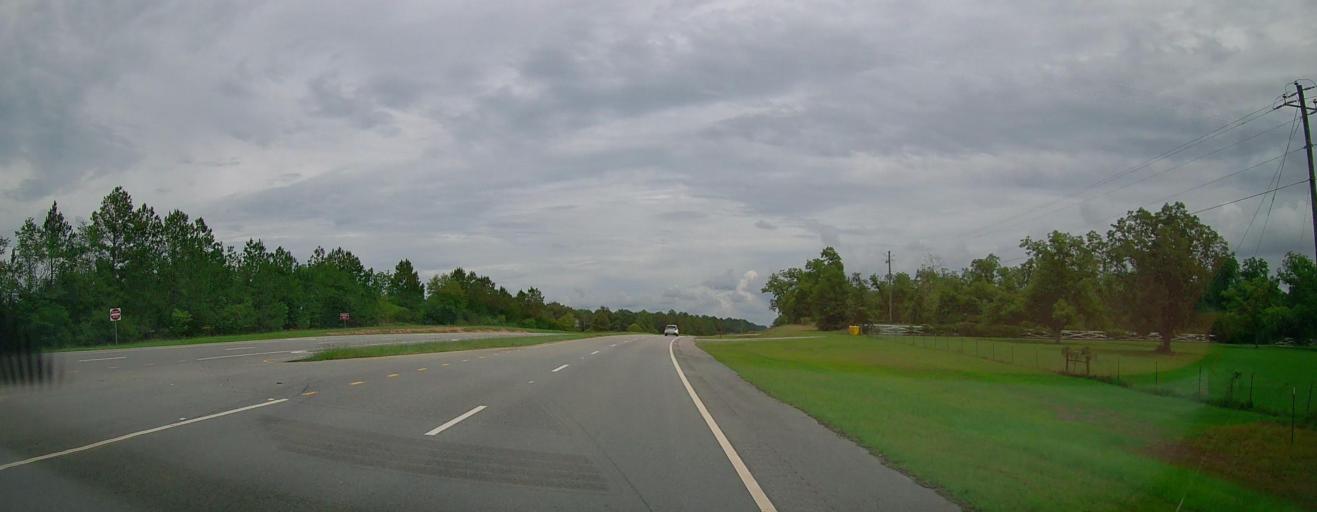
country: US
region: Georgia
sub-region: Telfair County
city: Helena
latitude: 32.1026
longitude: -82.9594
